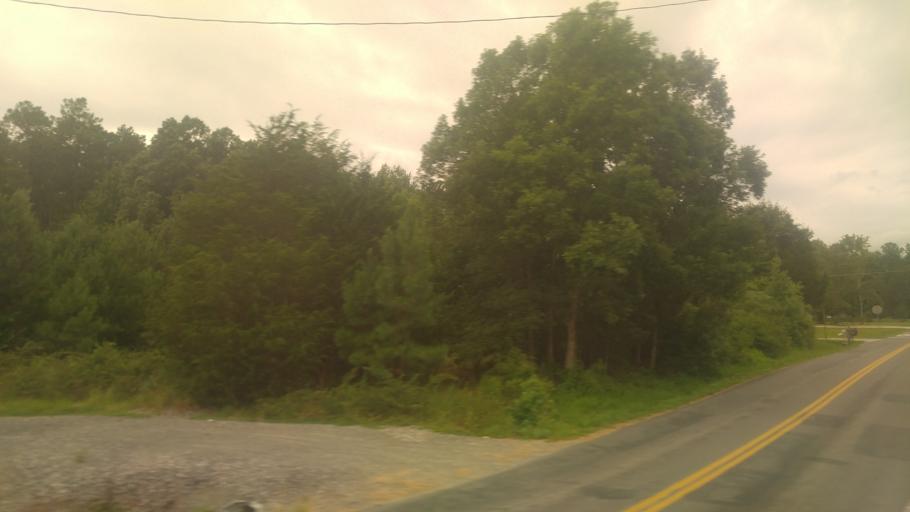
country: US
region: Virginia
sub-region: Hanover County
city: Ashland
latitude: 37.7141
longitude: -77.4952
